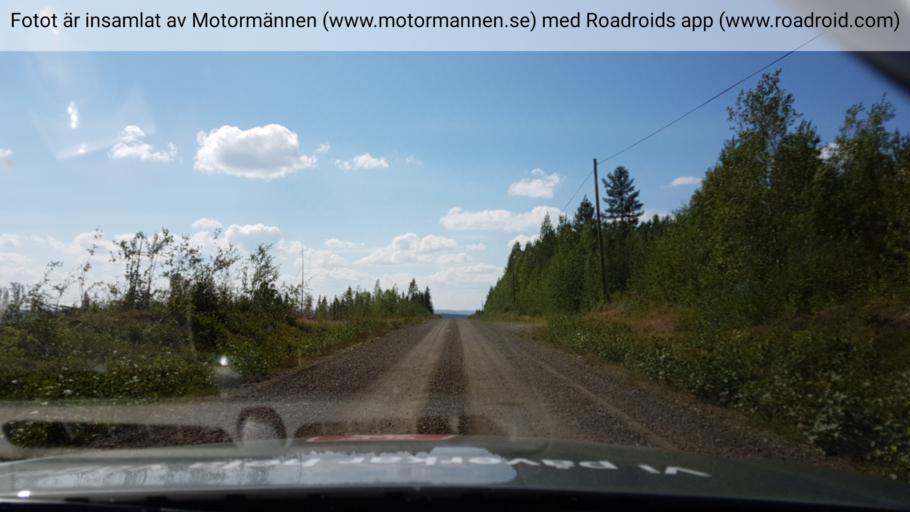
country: SE
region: Vaesterbotten
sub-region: Dorotea Kommun
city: Dorotea
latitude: 64.0957
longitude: 16.4434
